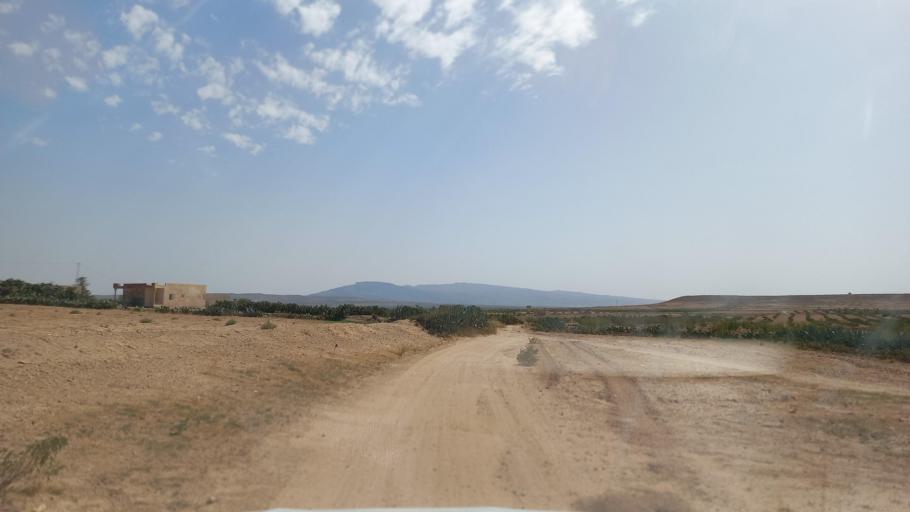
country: TN
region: Al Qasrayn
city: Kasserine
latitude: 35.2774
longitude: 8.9698
